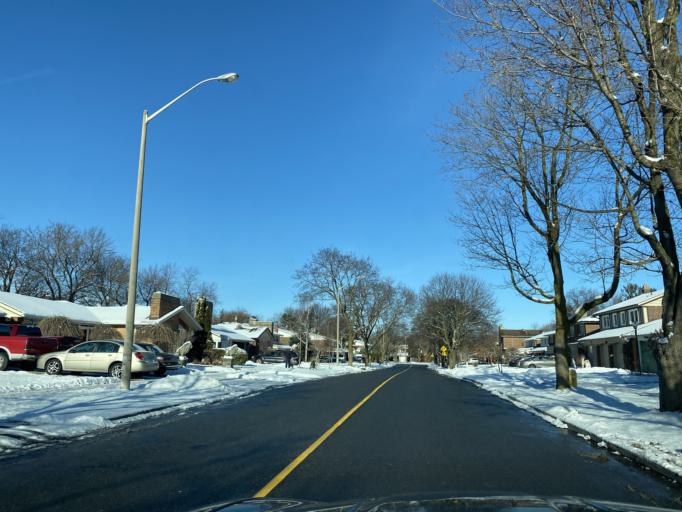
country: CA
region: Ontario
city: Scarborough
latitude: 43.7775
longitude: -79.3157
